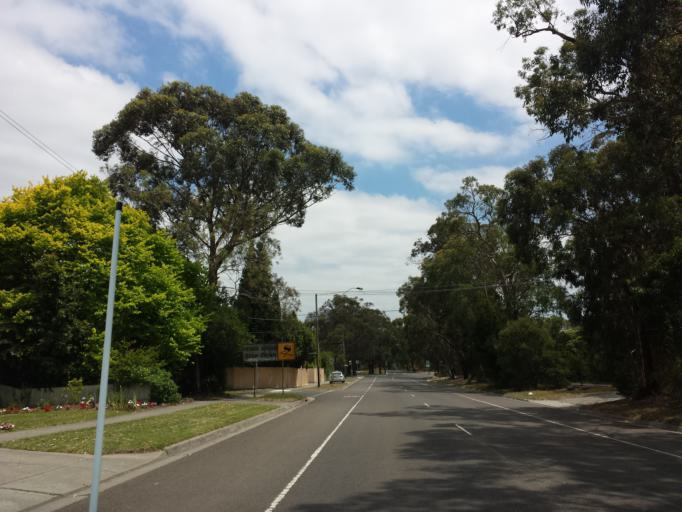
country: AU
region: Victoria
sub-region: Knox
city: Ferntree Gully
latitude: -37.8725
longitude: 145.2979
